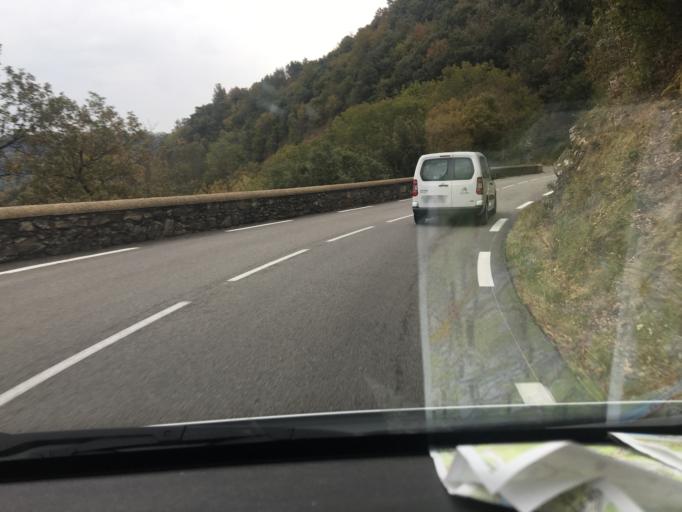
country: FR
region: Rhone-Alpes
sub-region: Departement de l'Ardeche
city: Saint-Jean-de-Muzols
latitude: 45.0661
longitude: 4.7552
